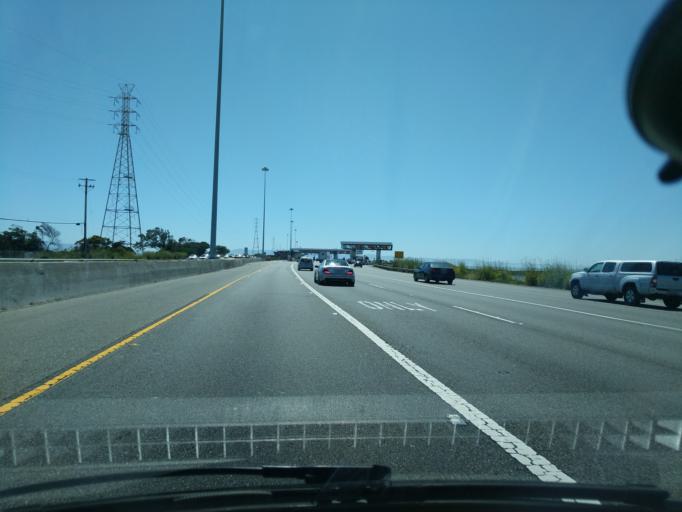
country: US
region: California
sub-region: Alameda County
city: San Lorenzo
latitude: 37.6191
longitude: -122.1485
